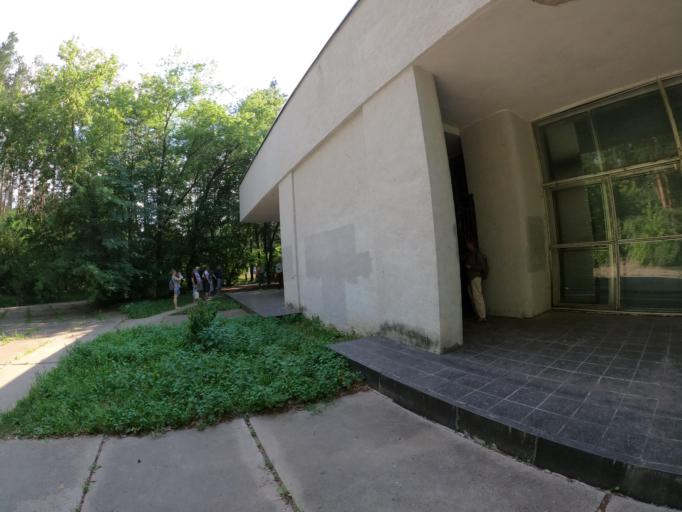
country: RU
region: Moskovskaya
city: Protvino
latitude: 54.8669
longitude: 37.2198
